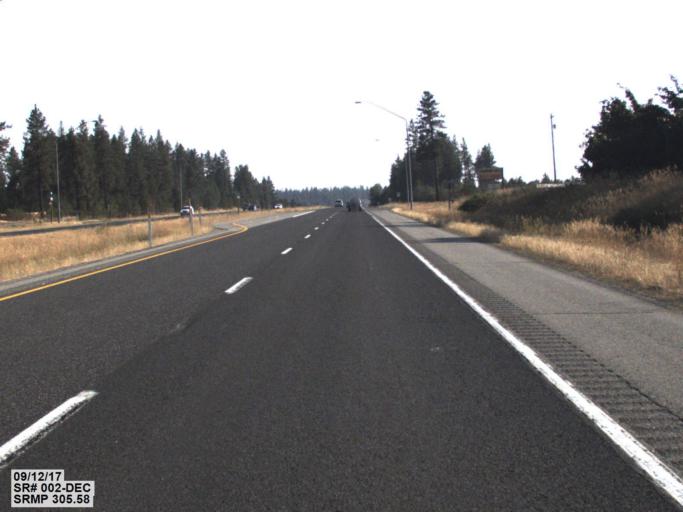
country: US
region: Washington
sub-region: Spokane County
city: Deer Park
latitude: 47.9050
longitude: -117.3513
